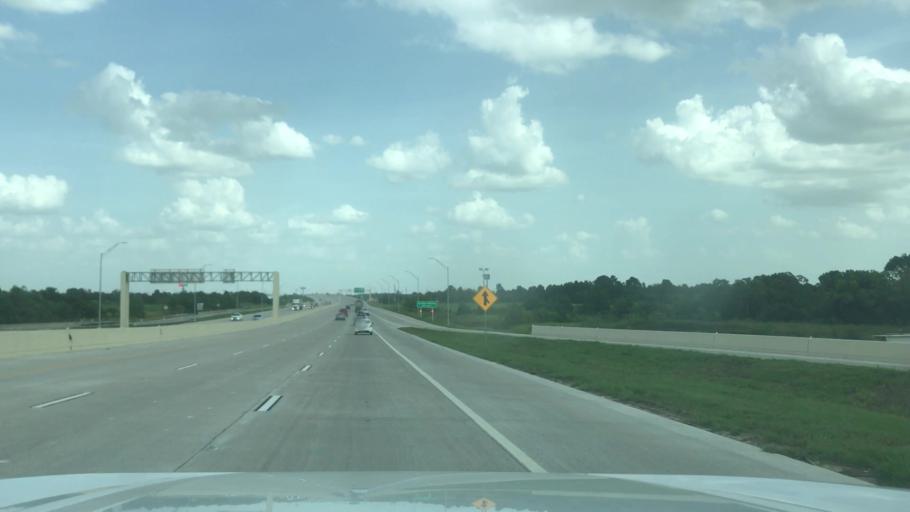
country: US
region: Texas
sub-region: Waller County
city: Waller
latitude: 30.0677
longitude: -95.9189
